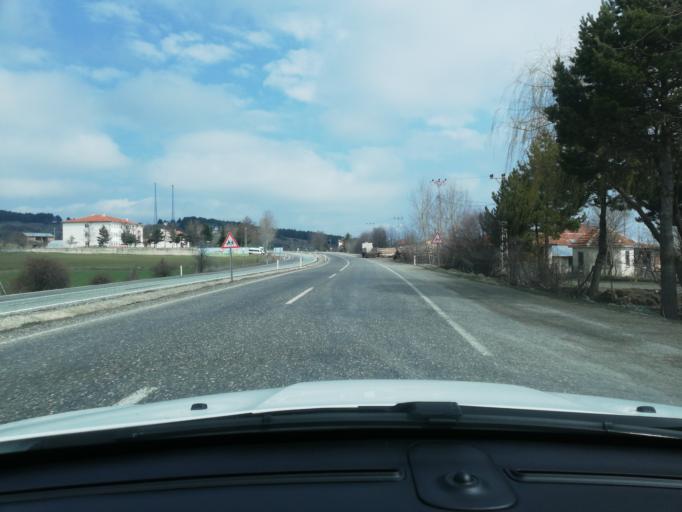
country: TR
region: Kastamonu
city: Kuzyaka
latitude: 41.2306
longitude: 33.7936
